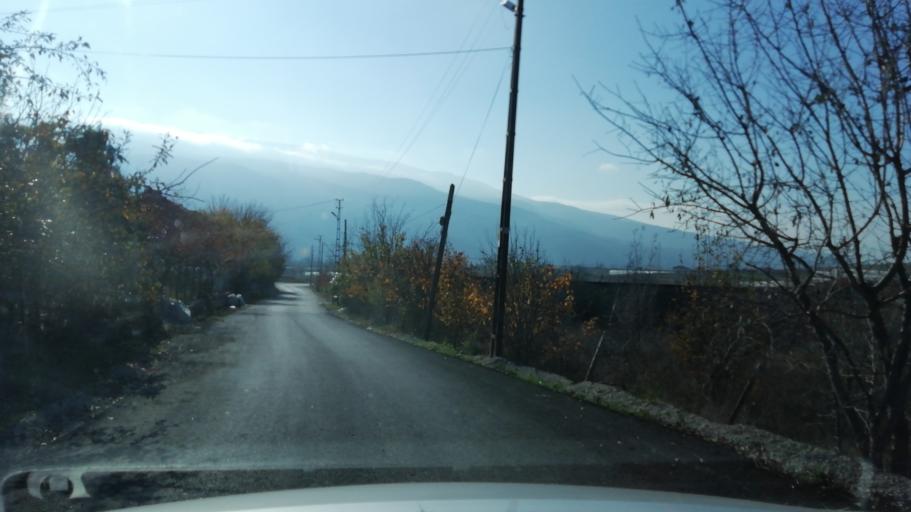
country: TR
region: Karabuk
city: Safranbolu
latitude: 41.2274
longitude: 32.7842
